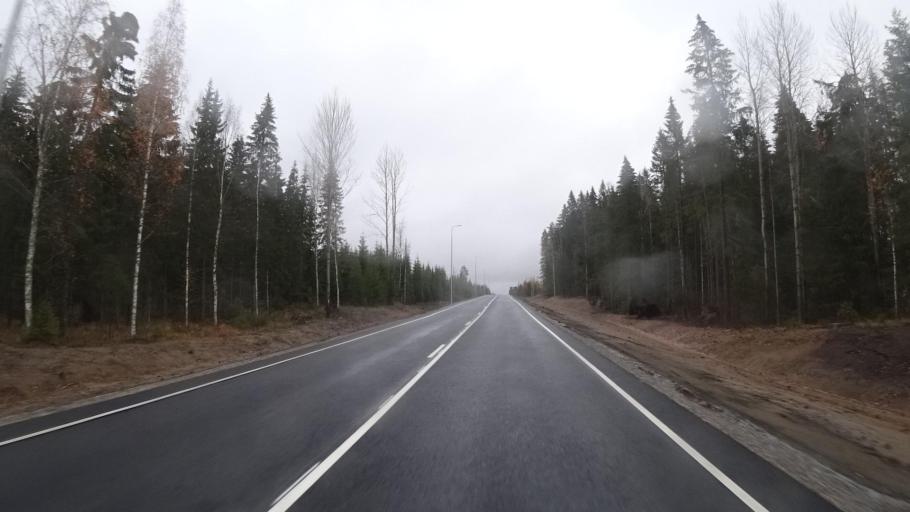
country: FI
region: Northern Savo
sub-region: Varkaus
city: Kangaslampi
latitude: 62.3807
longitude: 28.1267
